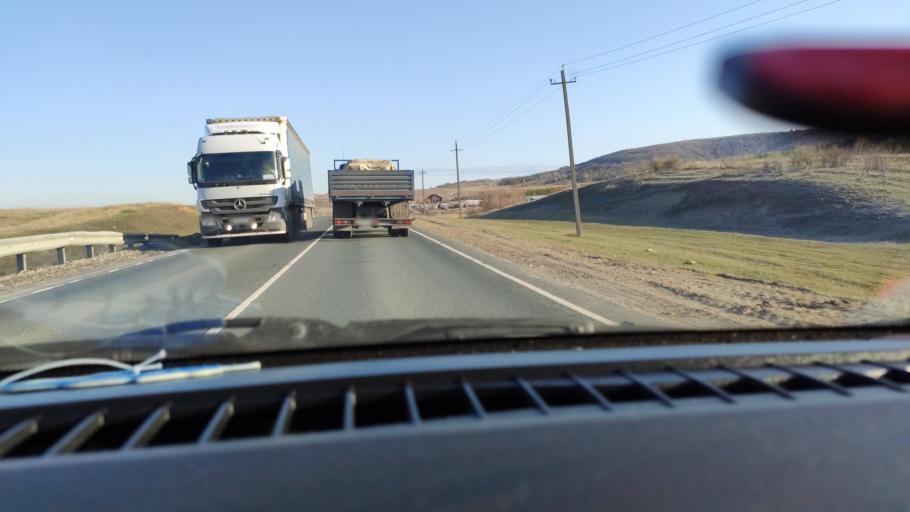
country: RU
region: Saratov
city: Alekseyevka
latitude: 52.3041
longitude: 47.9266
